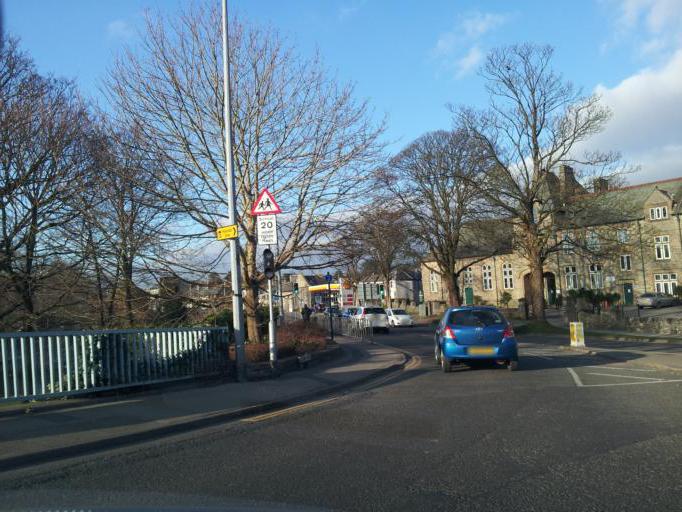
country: GB
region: England
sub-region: Cumbria
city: Kendal
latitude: 54.3170
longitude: -2.7419
